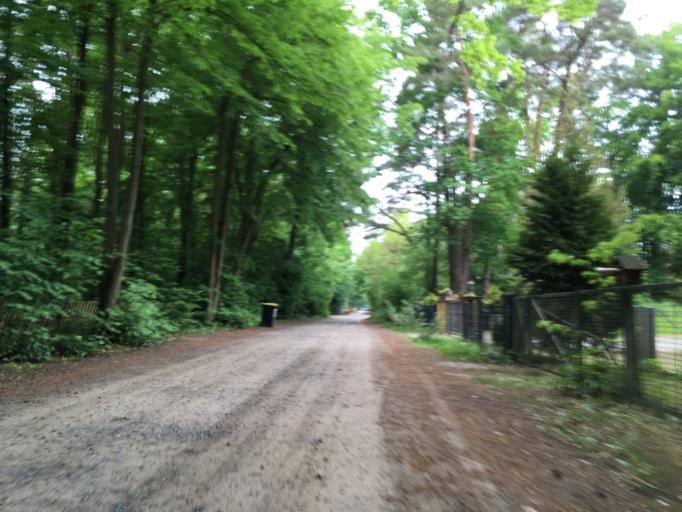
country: DE
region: Brandenburg
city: Wandlitz
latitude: 52.7501
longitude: 13.4866
